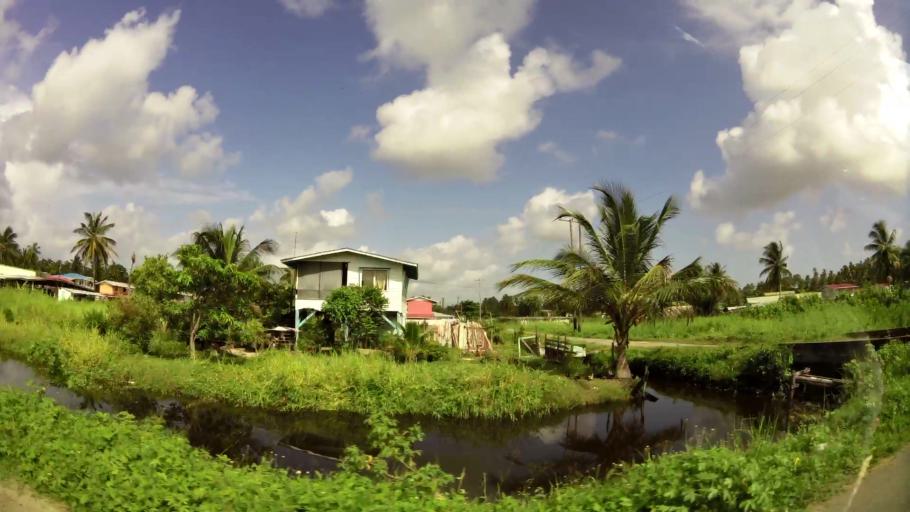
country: GY
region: Demerara-Mahaica
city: Mahaica Village
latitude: 6.7075
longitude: -57.9280
